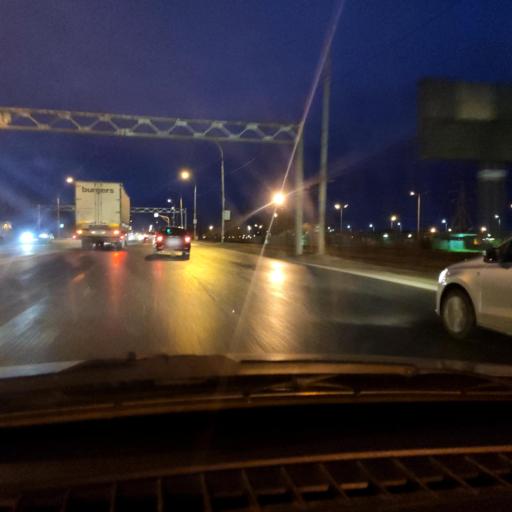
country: RU
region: Samara
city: Tol'yatti
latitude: 53.5646
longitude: 49.2903
